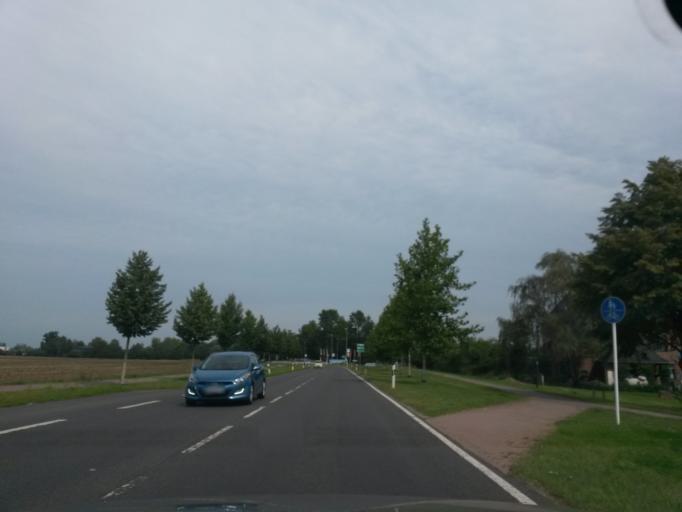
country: DE
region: Brandenburg
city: Schwedt (Oder)
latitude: 53.0470
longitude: 14.2678
